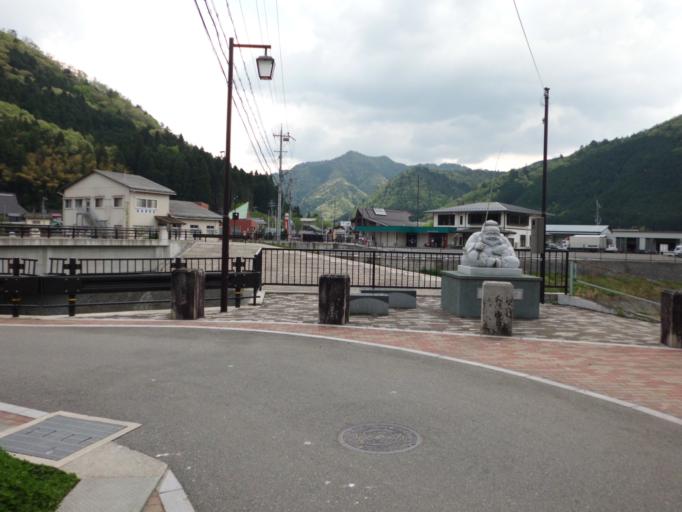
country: JP
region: Kyoto
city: Kameoka
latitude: 35.2744
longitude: 135.5506
